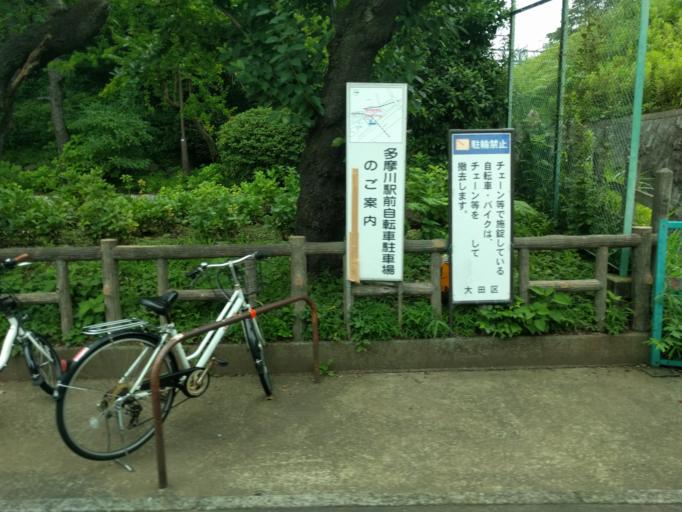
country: JP
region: Kanagawa
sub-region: Kawasaki-shi
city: Kawasaki
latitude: 35.5877
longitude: 139.6680
